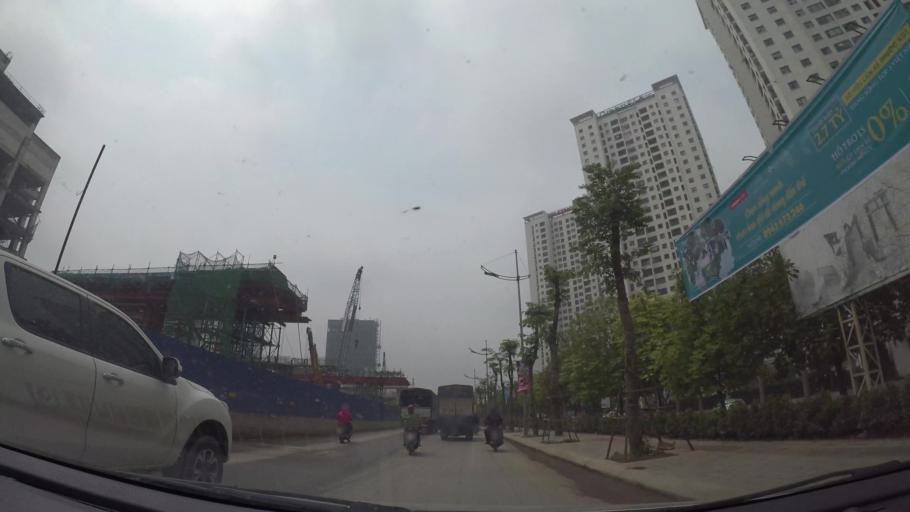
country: VN
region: Ha Noi
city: Cau Dien
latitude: 21.0535
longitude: 105.7816
